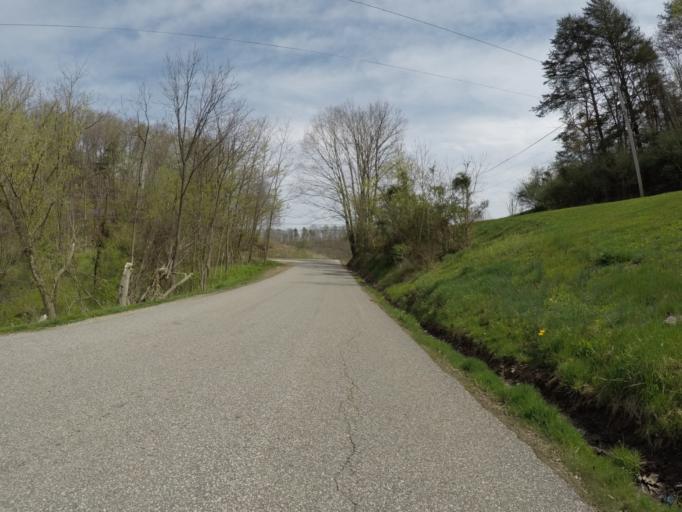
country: US
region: West Virginia
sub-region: Cabell County
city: Pea Ridge
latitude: 38.3439
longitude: -82.3594
